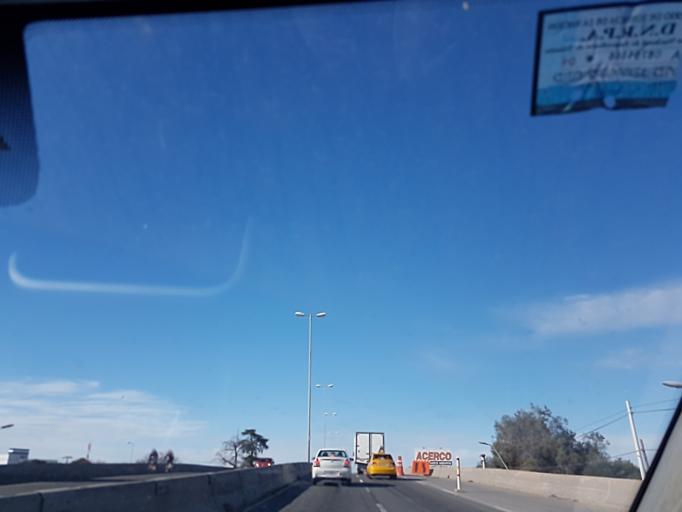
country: AR
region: Cordoba
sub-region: Departamento de Capital
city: Cordoba
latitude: -31.3342
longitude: -64.2090
